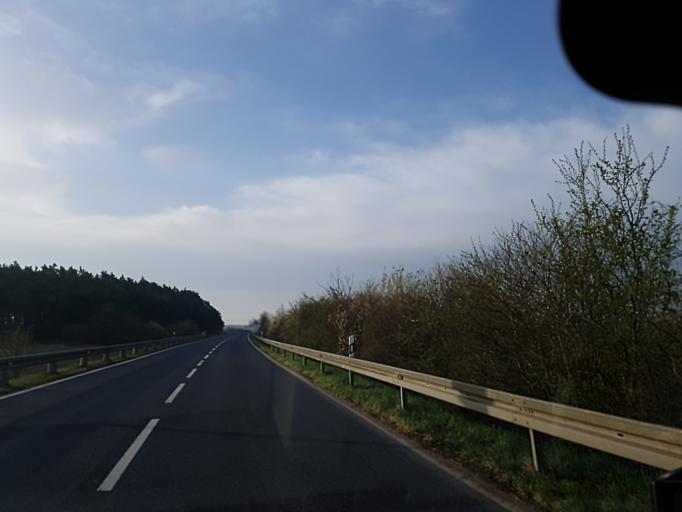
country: DE
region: Saxony
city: Riesa
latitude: 51.3450
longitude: 13.2971
